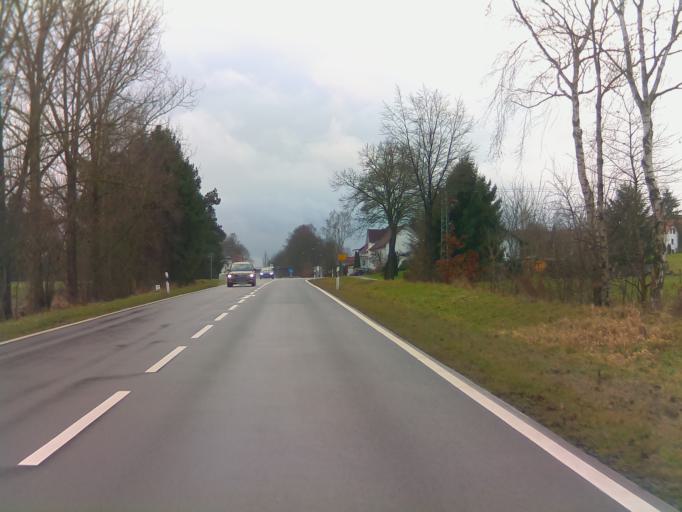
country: DE
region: Hesse
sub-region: Regierungsbezirk Kassel
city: Flieden
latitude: 50.4040
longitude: 9.5480
